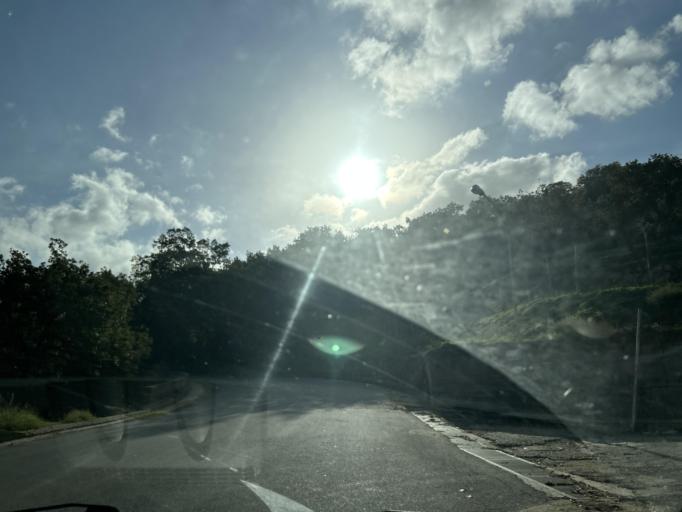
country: IT
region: Calabria
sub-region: Provincia di Catanzaro
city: Montepaone
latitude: 38.7225
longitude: 16.5087
